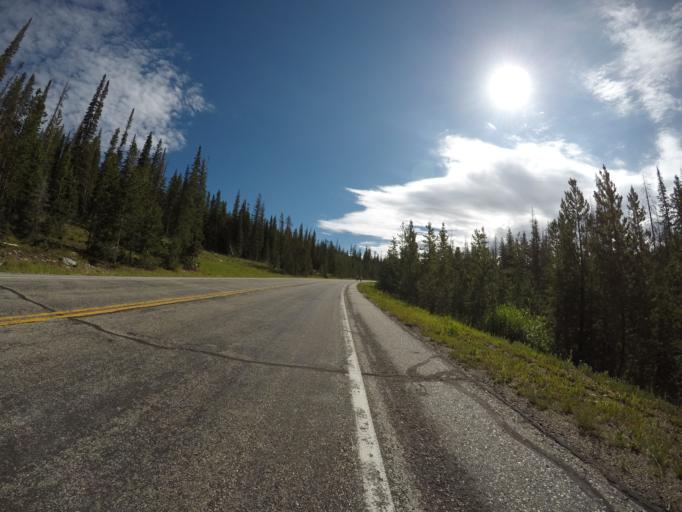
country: US
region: Wyoming
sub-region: Carbon County
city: Saratoga
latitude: 41.3259
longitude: -106.4433
